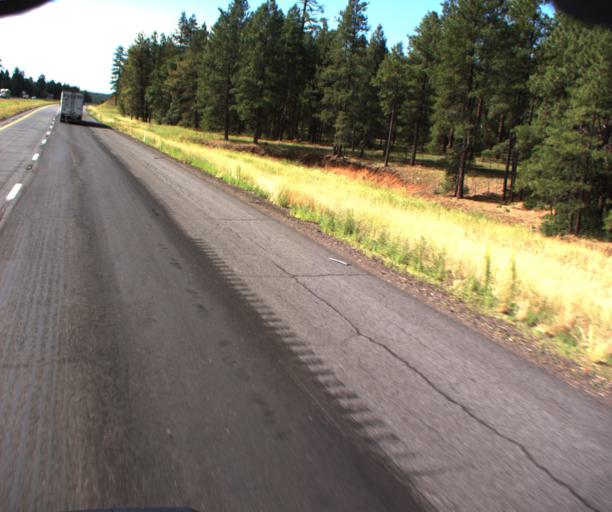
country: US
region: Arizona
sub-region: Coconino County
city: Mountainaire
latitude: 34.9697
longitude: -111.6839
